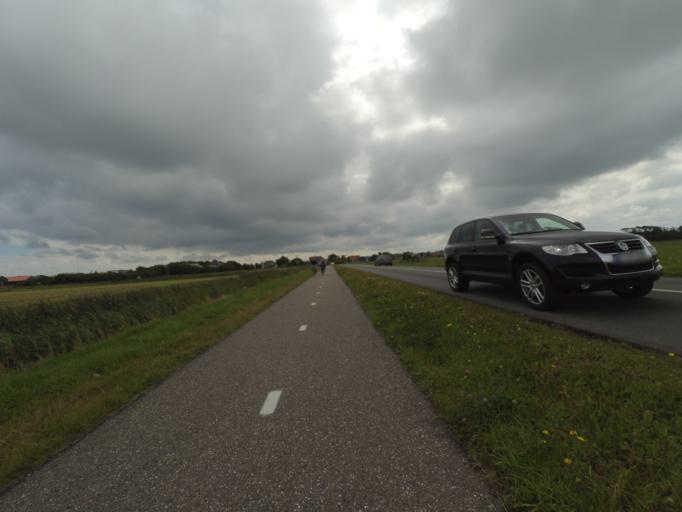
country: NL
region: North Holland
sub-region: Gemeente Texel
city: Den Burg
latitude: 53.0419
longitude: 4.8389
